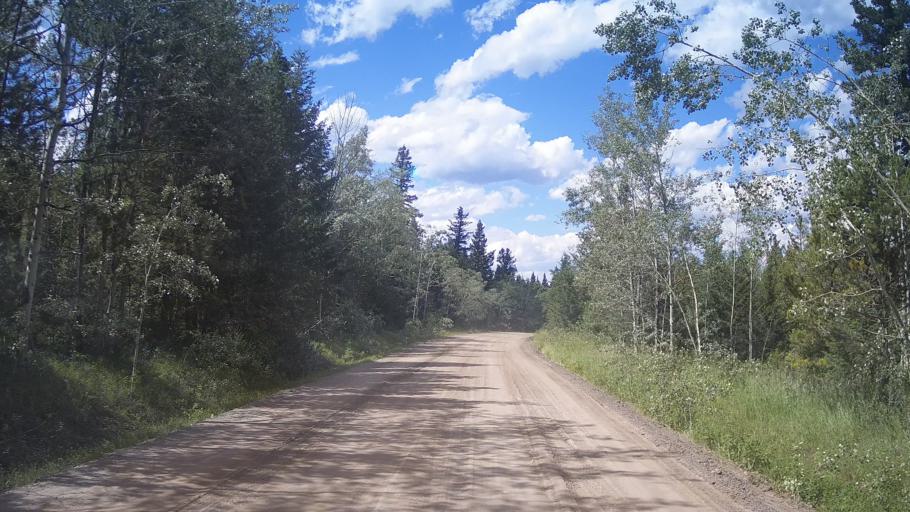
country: CA
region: British Columbia
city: Lillooet
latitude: 51.3300
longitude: -121.8931
